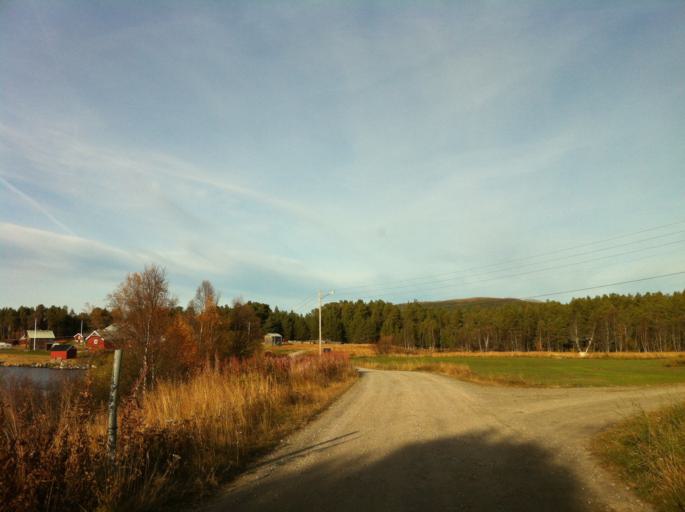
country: NO
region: Hedmark
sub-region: Engerdal
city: Engerdal
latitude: 62.1677
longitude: 11.9416
